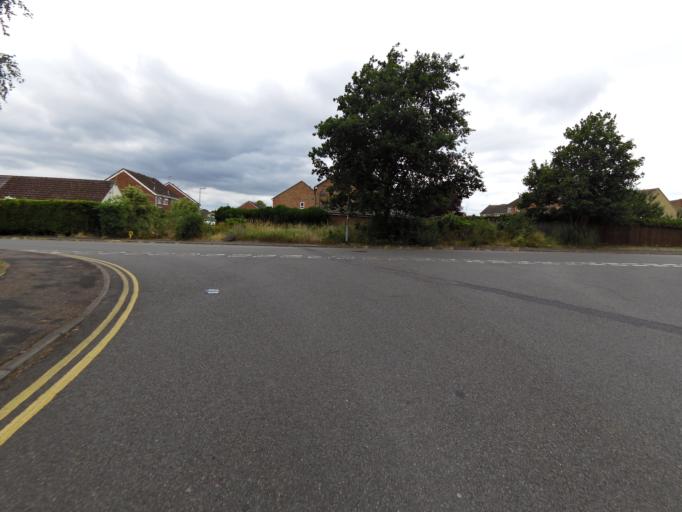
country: GB
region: England
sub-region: Norfolk
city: Diss
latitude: 52.3742
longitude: 1.1212
